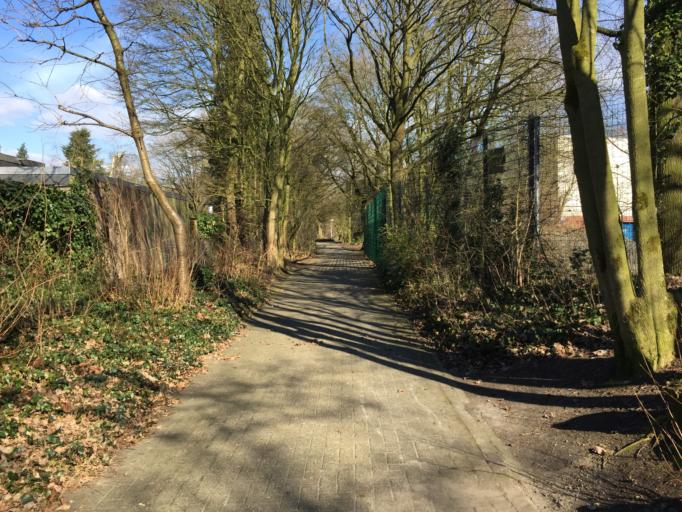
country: DE
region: Lower Saxony
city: Oldenburg
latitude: 53.1639
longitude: 8.2304
